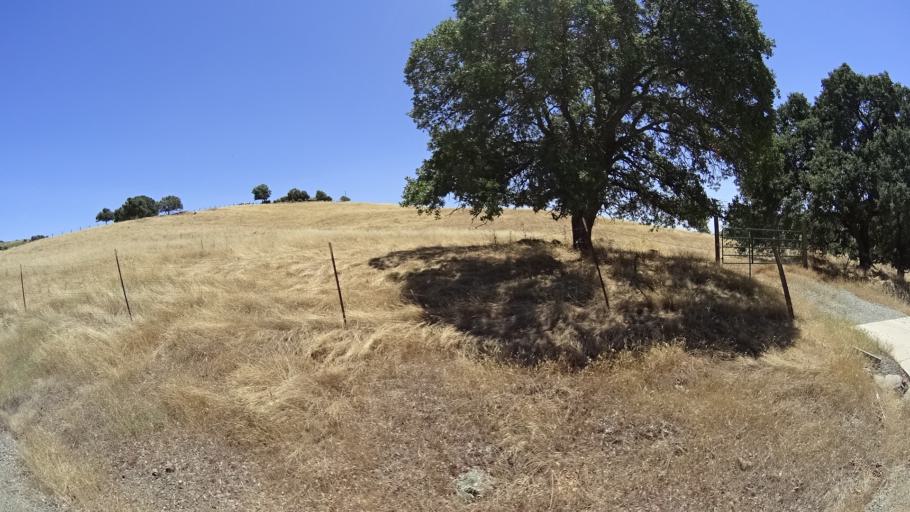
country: US
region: California
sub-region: Calaveras County
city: Valley Springs
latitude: 38.2360
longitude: -120.7958
